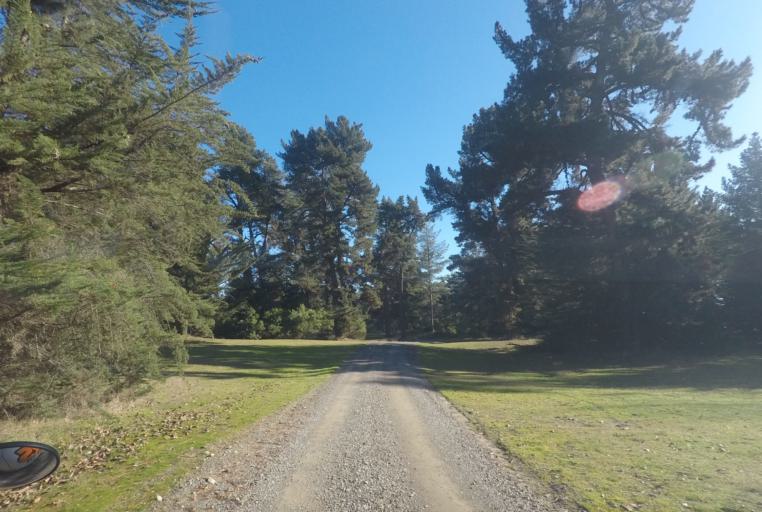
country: NZ
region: Tasman
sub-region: Tasman District
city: Mapua
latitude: -41.2633
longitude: 173.1440
